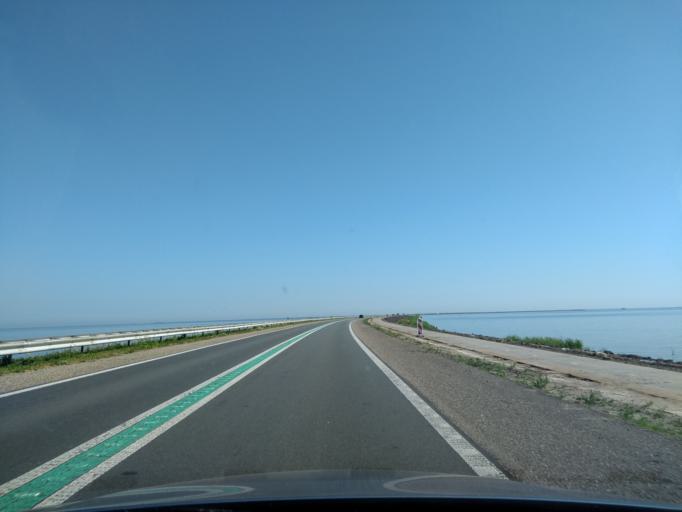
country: NL
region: Flevoland
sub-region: Gemeente Lelystad
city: Lelystad
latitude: 52.5369
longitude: 5.4271
